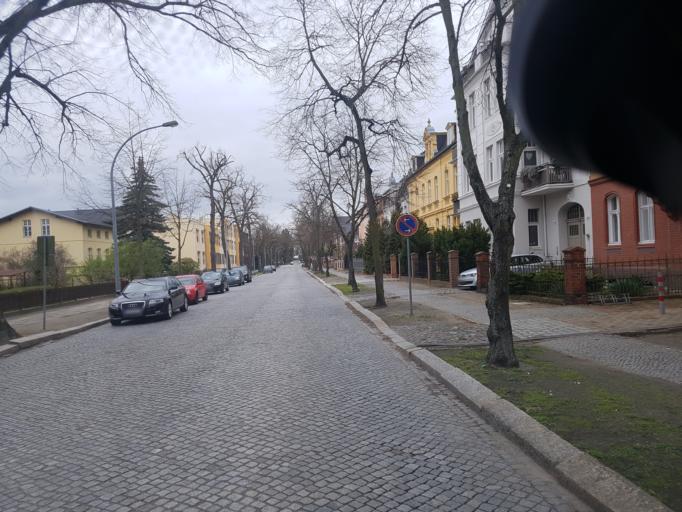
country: DE
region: Brandenburg
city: Luebben
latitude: 51.9372
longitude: 13.8877
